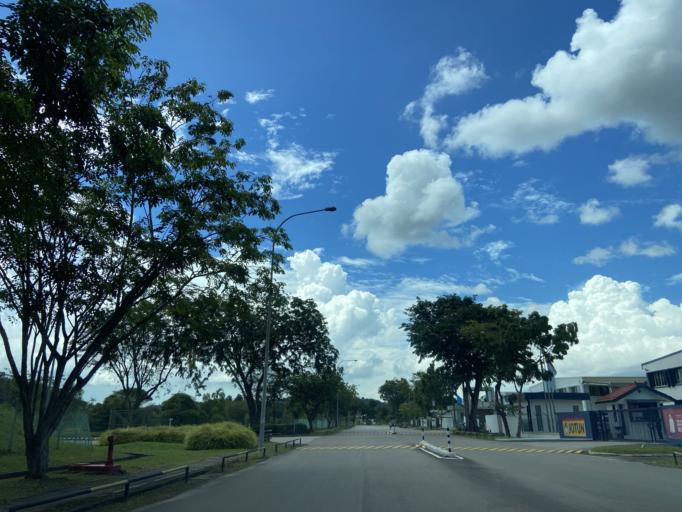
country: SG
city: Singapore
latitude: 1.0575
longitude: 104.0300
